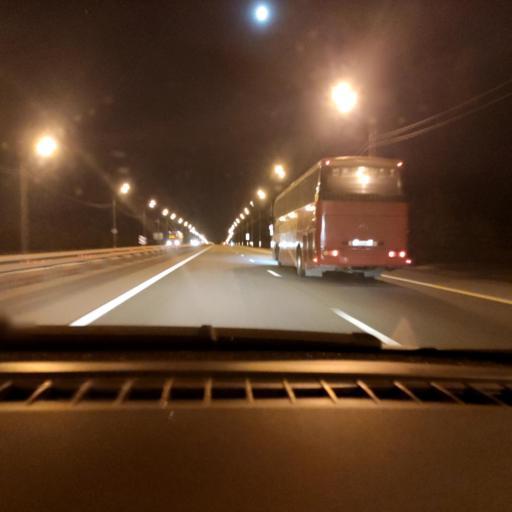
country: RU
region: Lipetsk
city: Khlevnoye
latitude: 52.2342
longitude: 39.0828
